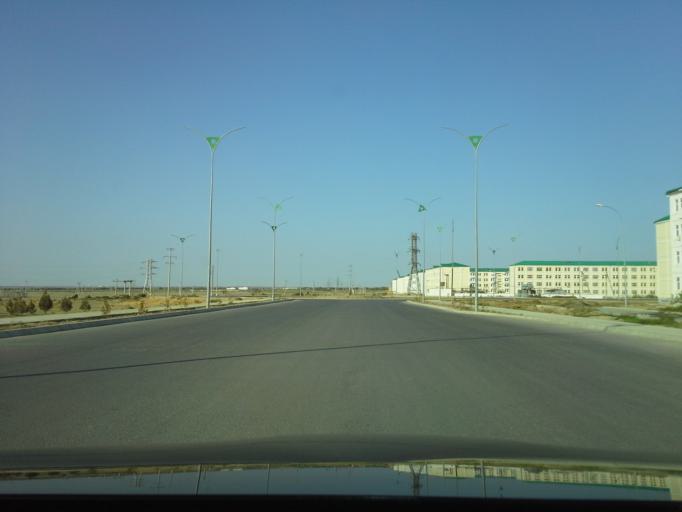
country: TM
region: Ahal
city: Abadan
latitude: 38.0561
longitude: 58.1382
